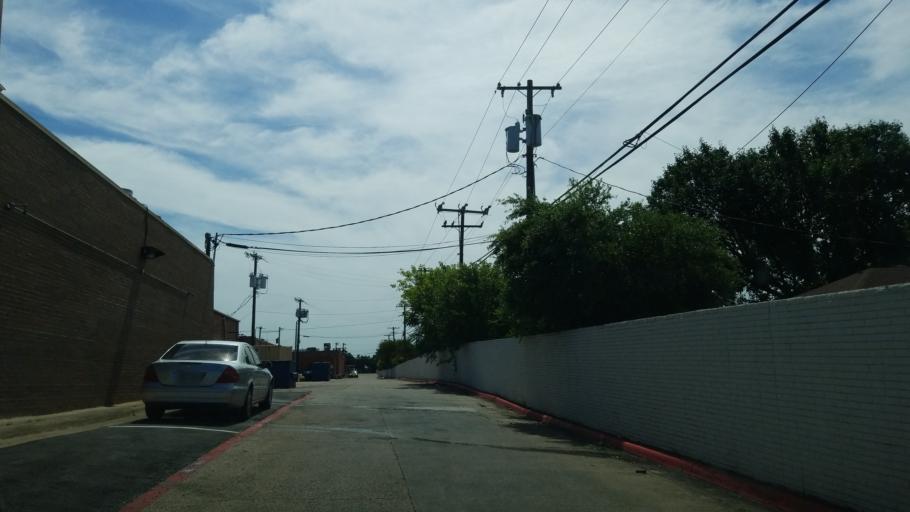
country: US
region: Texas
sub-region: Dallas County
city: Farmers Branch
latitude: 32.9081
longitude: -96.8558
